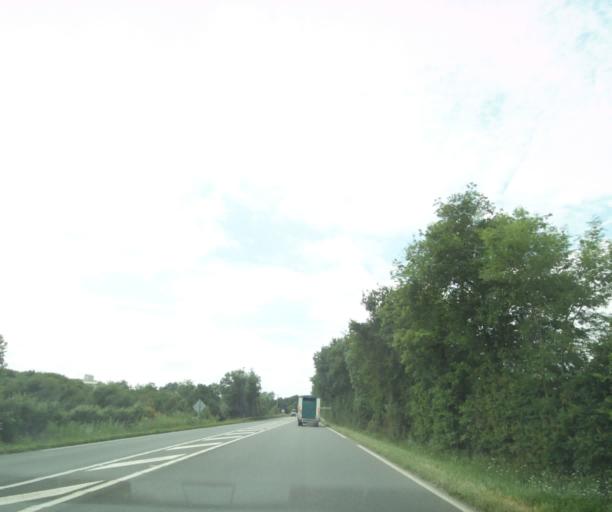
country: FR
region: Poitou-Charentes
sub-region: Departement des Deux-Sevres
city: Champdeniers-Saint-Denis
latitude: 46.4959
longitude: -0.3442
